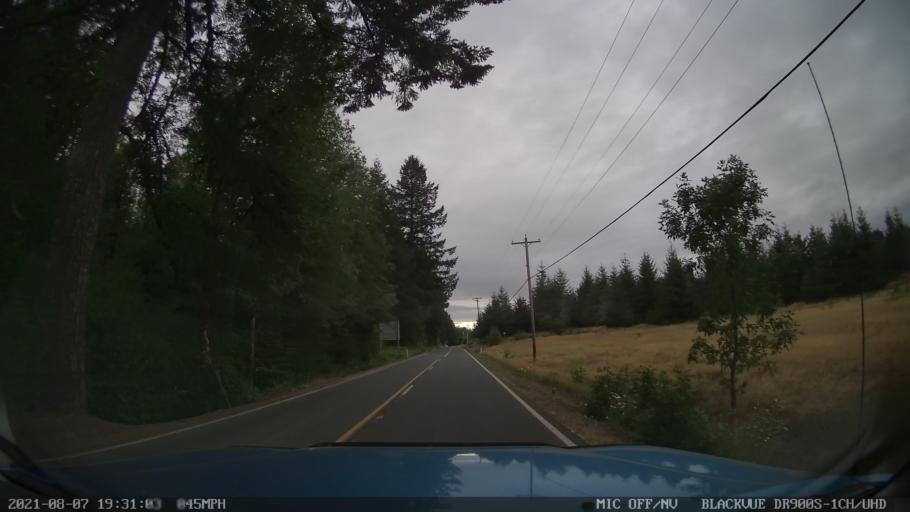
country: US
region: Oregon
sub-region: Linn County
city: Lyons
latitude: 44.8890
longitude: -122.6286
